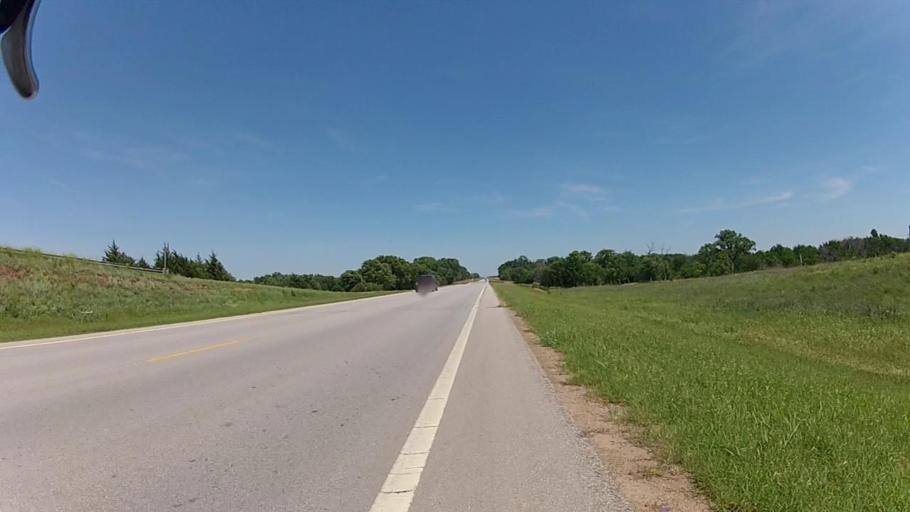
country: US
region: Kansas
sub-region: Harper County
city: Harper
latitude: 37.2390
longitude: -98.1653
